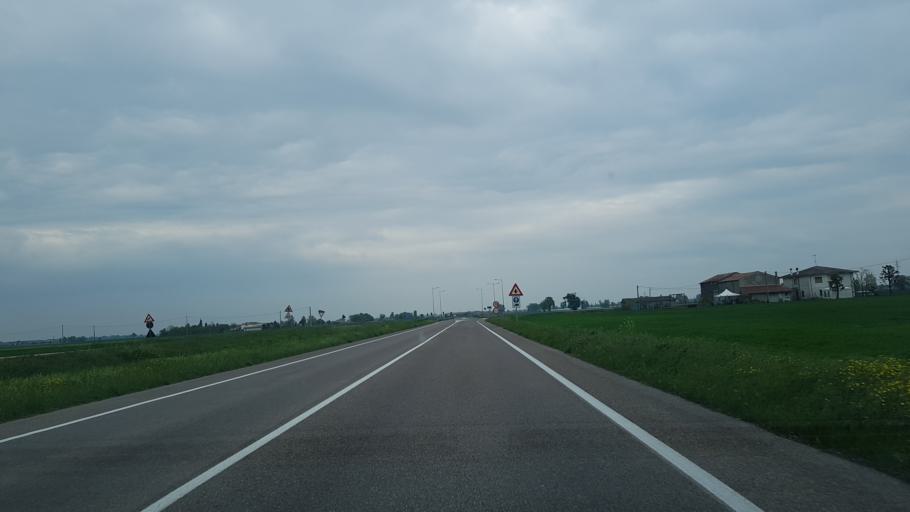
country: IT
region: Veneto
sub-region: Provincia di Rovigo
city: Melara
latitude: 45.0749
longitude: 11.2225
